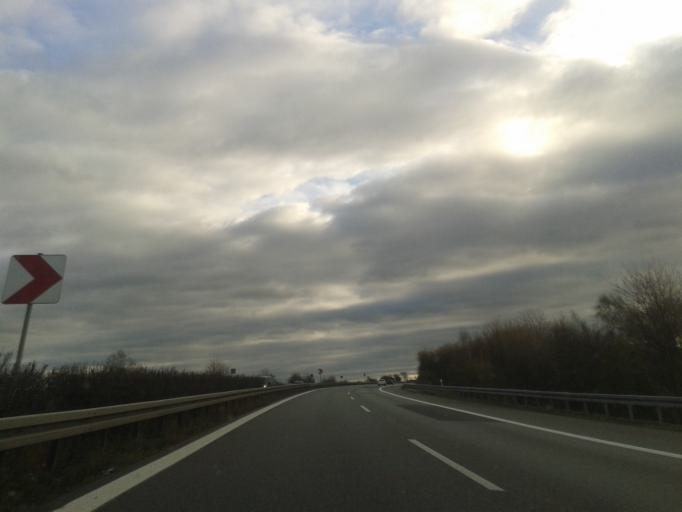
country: DE
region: Saxony
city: Wachau
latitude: 51.1696
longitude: 13.9146
